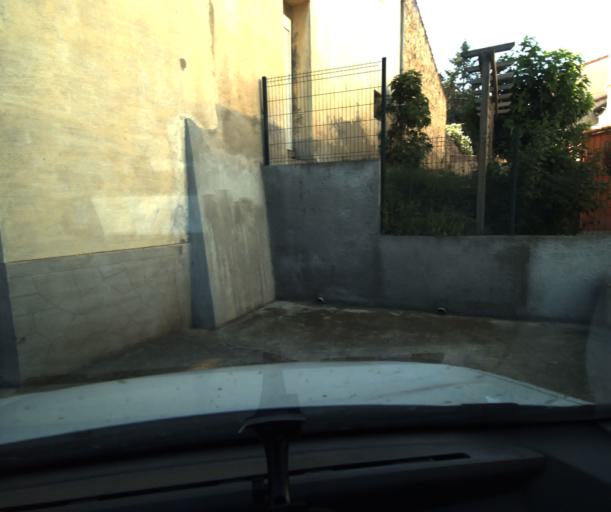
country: FR
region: Languedoc-Roussillon
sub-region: Departement des Pyrenees-Orientales
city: el Volo
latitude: 42.5256
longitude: 2.8356
